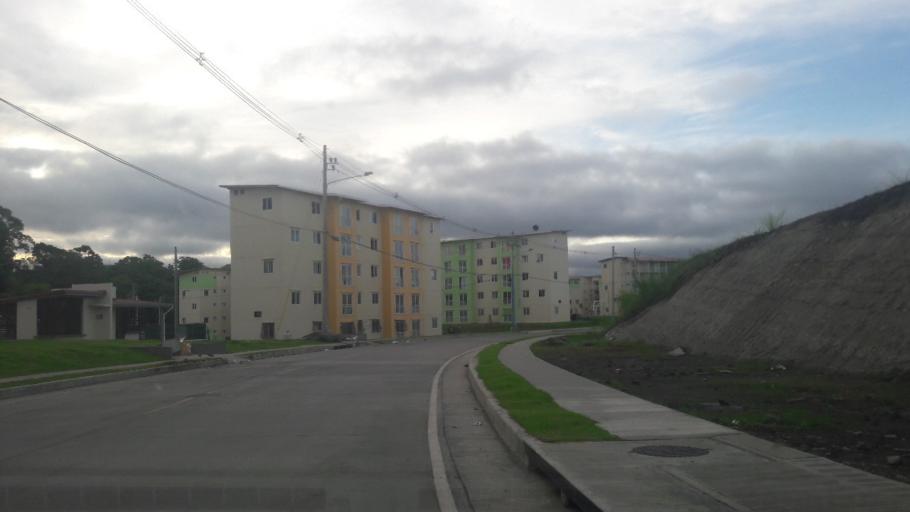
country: PA
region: Colon
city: Cativa
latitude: 9.3711
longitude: -79.8496
